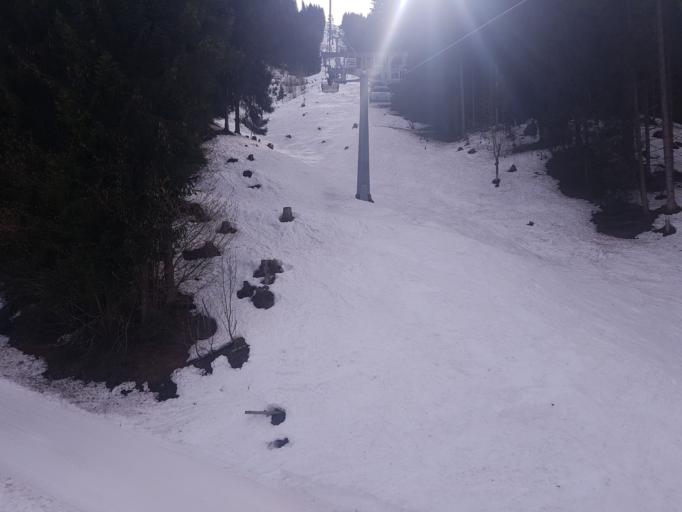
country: AT
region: Tyrol
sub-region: Politischer Bezirk Kufstein
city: Worgl
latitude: 47.4444
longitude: 12.0868
